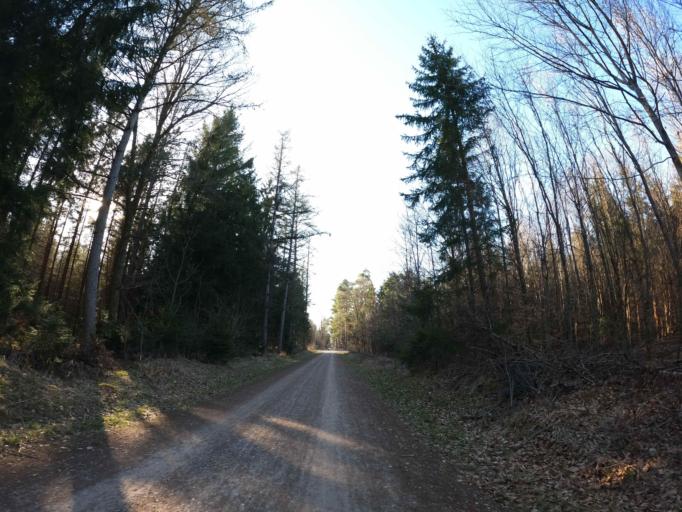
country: DE
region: Bavaria
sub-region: Upper Bavaria
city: Unterhaching
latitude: 48.0754
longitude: 11.5812
